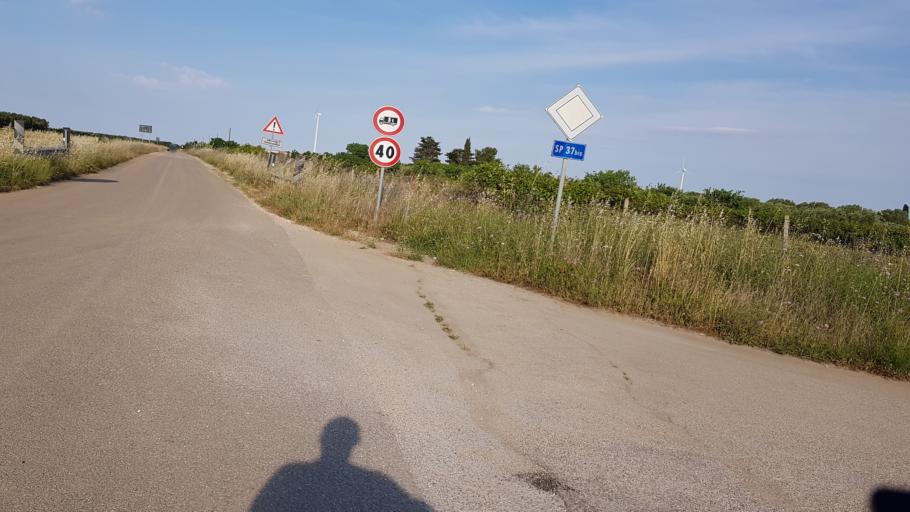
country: IT
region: Apulia
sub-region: Provincia di Brindisi
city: Mesagne
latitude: 40.6196
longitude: 17.7846
